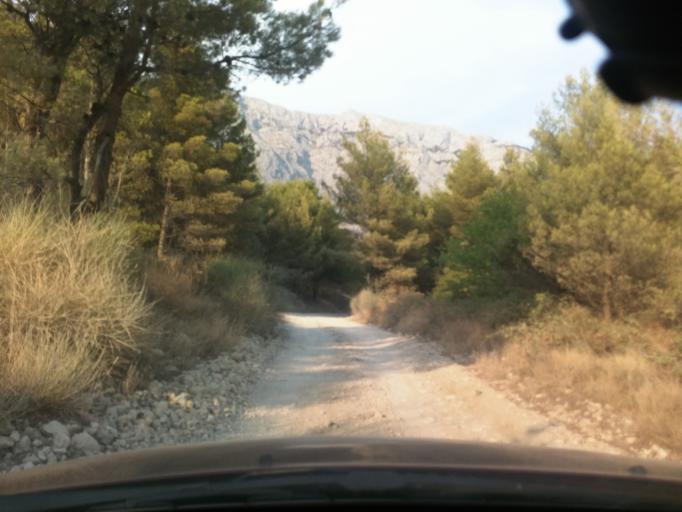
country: HR
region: Splitsko-Dalmatinska
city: Baska Voda
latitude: 43.3509
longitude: 16.9572
